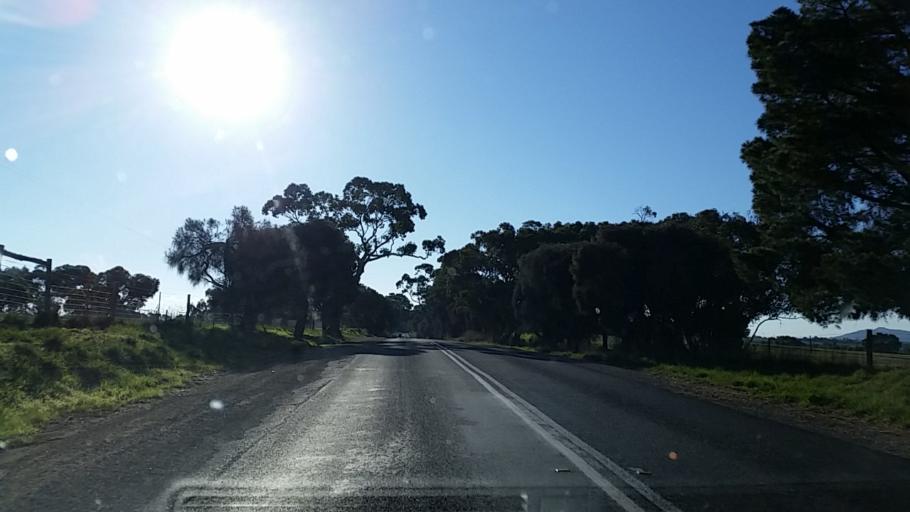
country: AU
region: South Australia
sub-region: Mount Barker
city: Macclesfield
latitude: -35.1426
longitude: 138.9221
